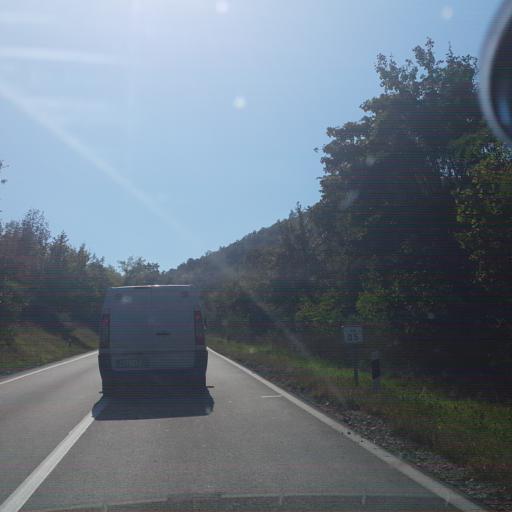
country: RS
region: Central Serbia
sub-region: Zajecarski Okrug
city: Knjazevac
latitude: 43.5369
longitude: 22.2275
